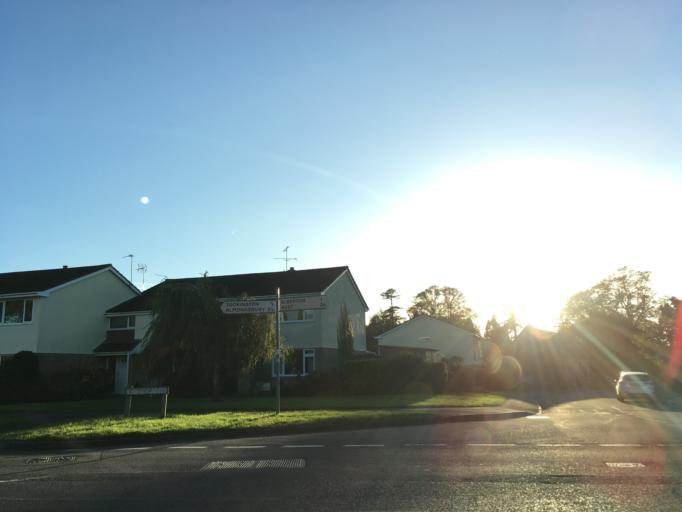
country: GB
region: England
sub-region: South Gloucestershire
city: Almondsbury
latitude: 51.5792
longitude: -2.5761
